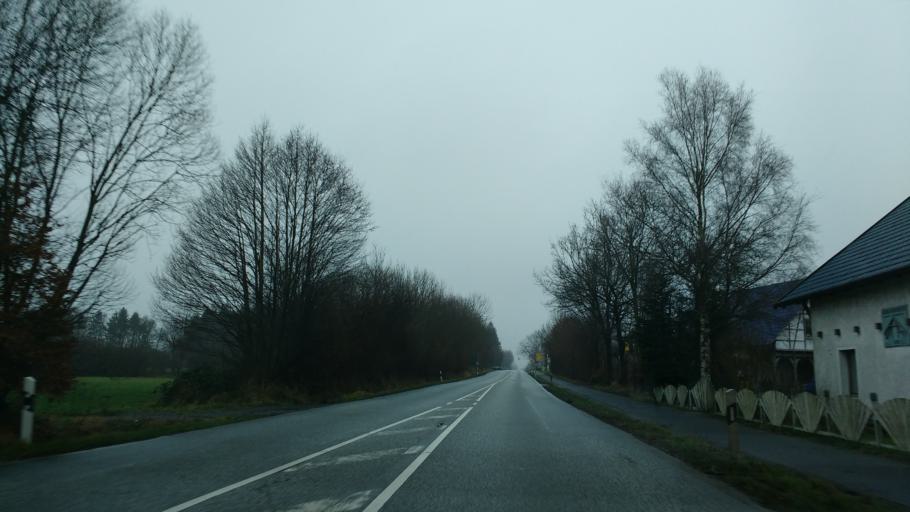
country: DE
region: Schleswig-Holstein
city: Brinjahe
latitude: 54.1801
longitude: 9.6351
